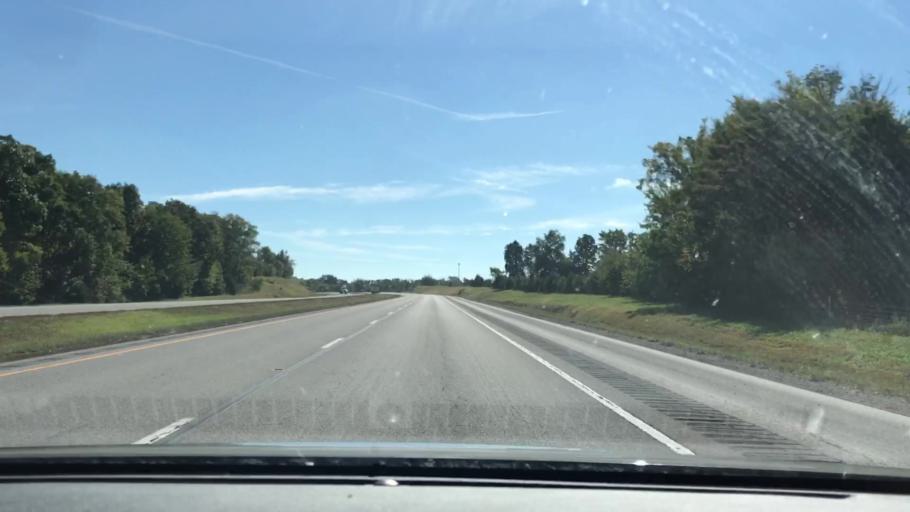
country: US
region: Kentucky
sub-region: Todd County
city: Elkton
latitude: 36.8293
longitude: -87.2254
